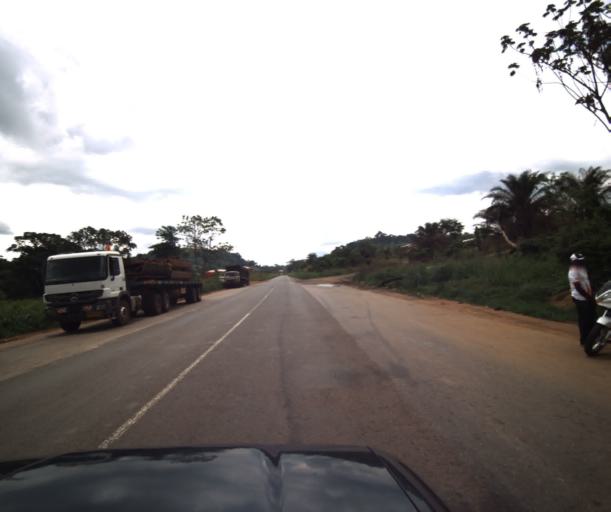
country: CM
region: Centre
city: Eseka
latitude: 3.8908
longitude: 10.7149
